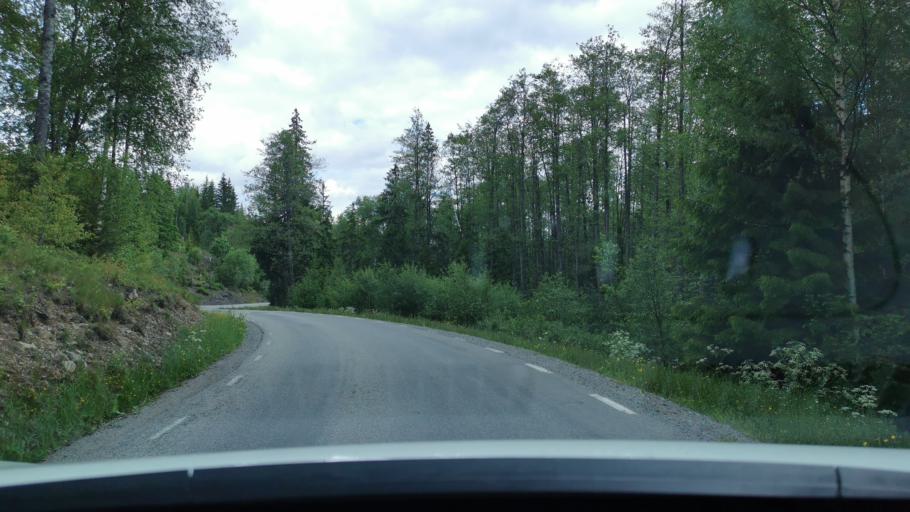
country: SE
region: Vaestra Goetaland
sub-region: Bengtsfors Kommun
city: Dals Langed
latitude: 58.8192
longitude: 12.3276
